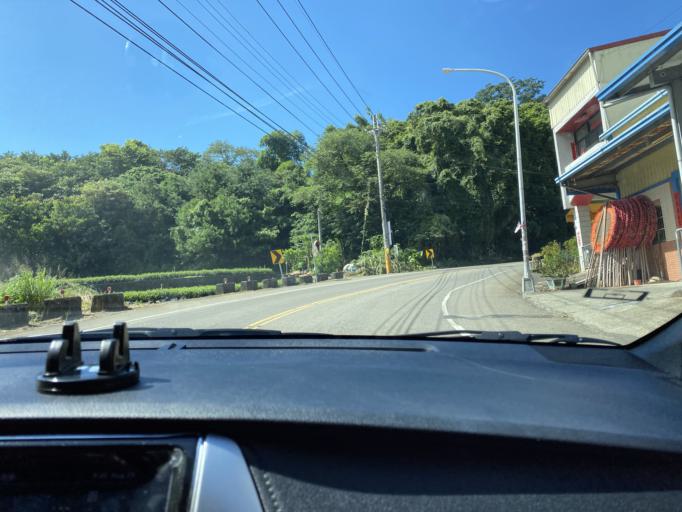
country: TW
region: Taiwan
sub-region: Nantou
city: Nantou
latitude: 23.8546
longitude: 120.6287
